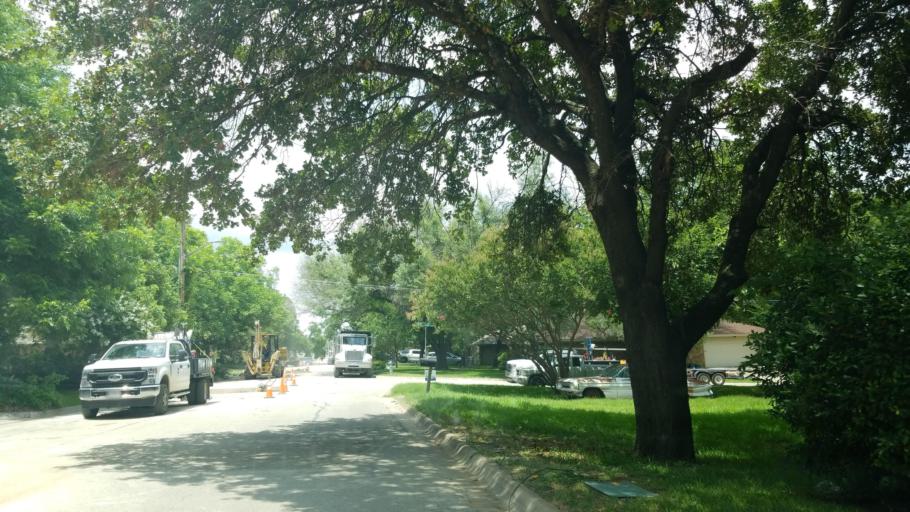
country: US
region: Texas
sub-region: Denton County
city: Denton
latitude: 33.2016
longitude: -97.1508
